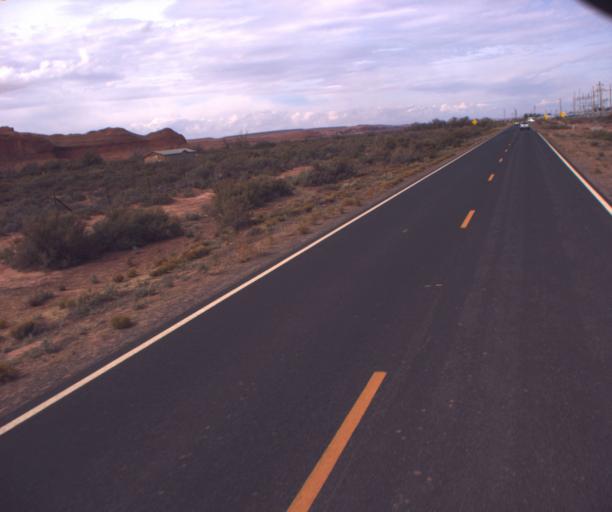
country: US
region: Arizona
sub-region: Apache County
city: Many Farms
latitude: 36.7097
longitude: -109.6226
